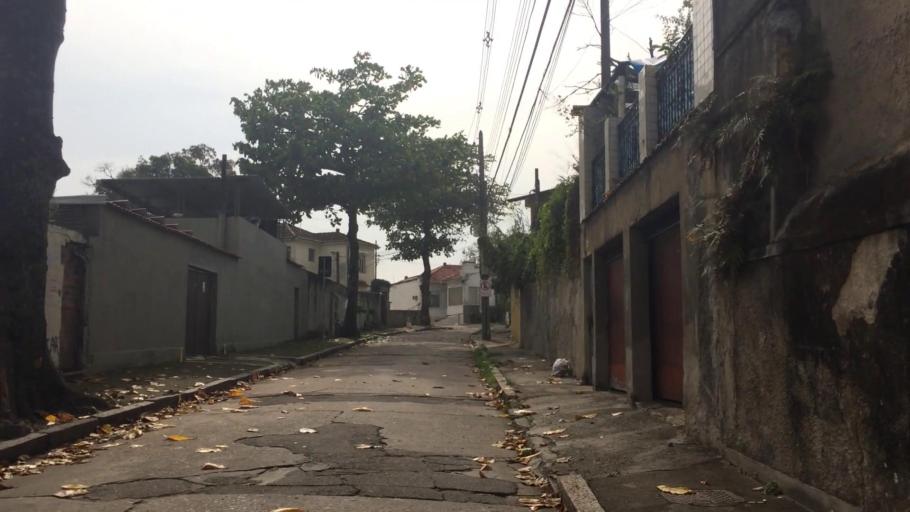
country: BR
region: Rio de Janeiro
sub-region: Rio De Janeiro
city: Rio de Janeiro
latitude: -22.9375
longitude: -43.1878
